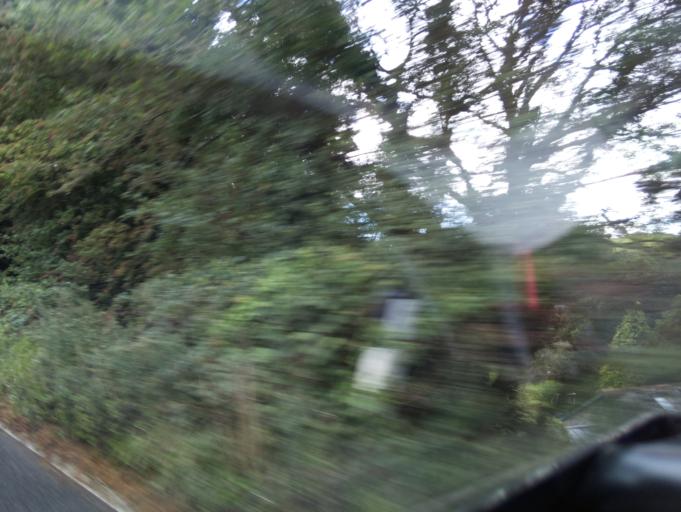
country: GB
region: England
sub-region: Devon
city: Modbury
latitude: 50.3238
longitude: -3.8432
